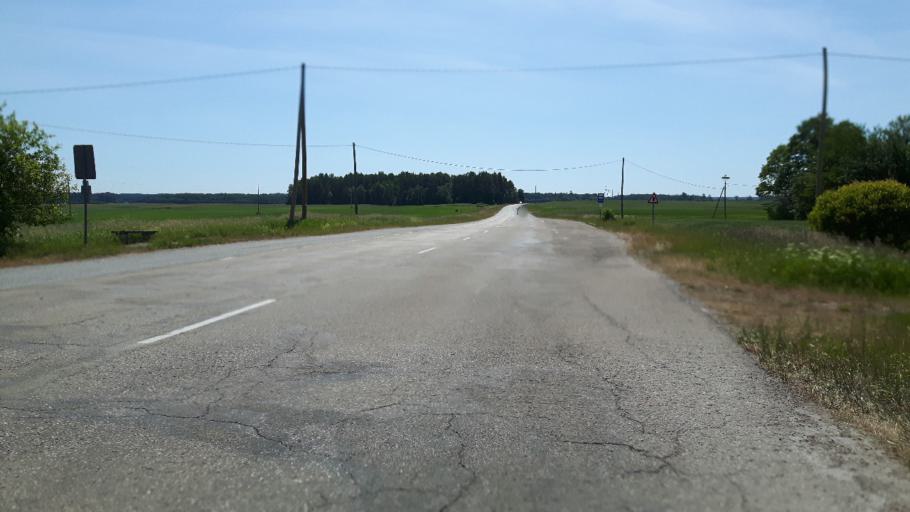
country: LV
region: Aizpute
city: Aizpute
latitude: 56.8287
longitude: 21.7447
